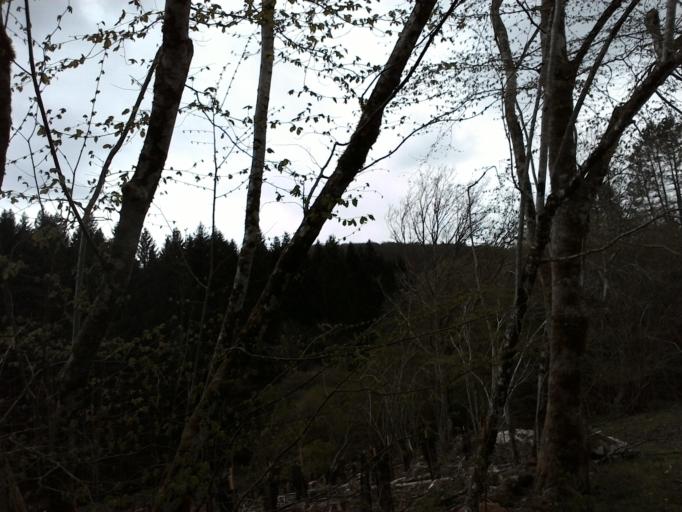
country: FR
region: Bourgogne
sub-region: Departement de la Cote-d'Or
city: Saulieu
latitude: 47.2451
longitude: 4.0628
